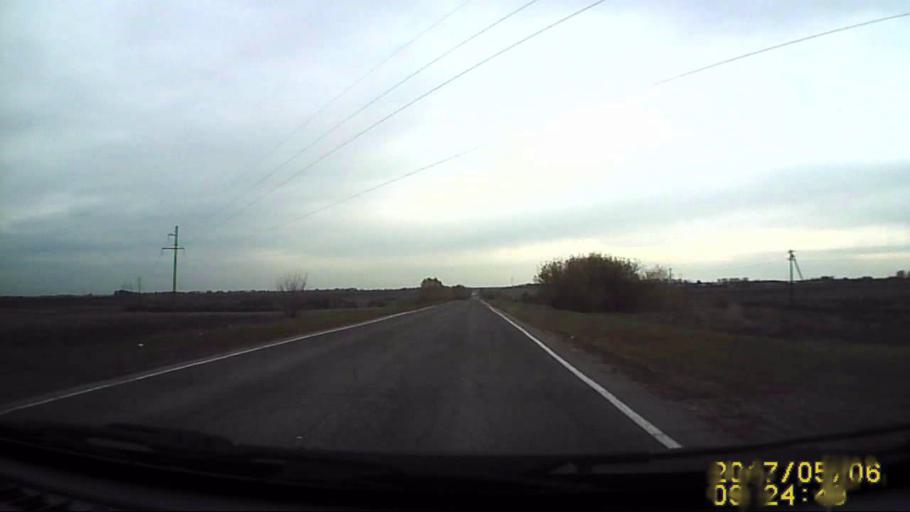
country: RU
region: Ulyanovsk
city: Cherdakly
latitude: 54.3807
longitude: 48.8121
